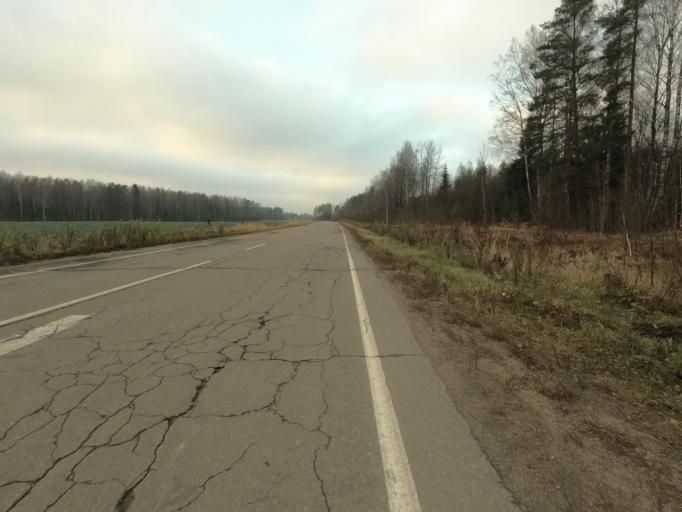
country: RU
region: Leningrad
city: Kirovsk
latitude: 59.7989
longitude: 31.0003
